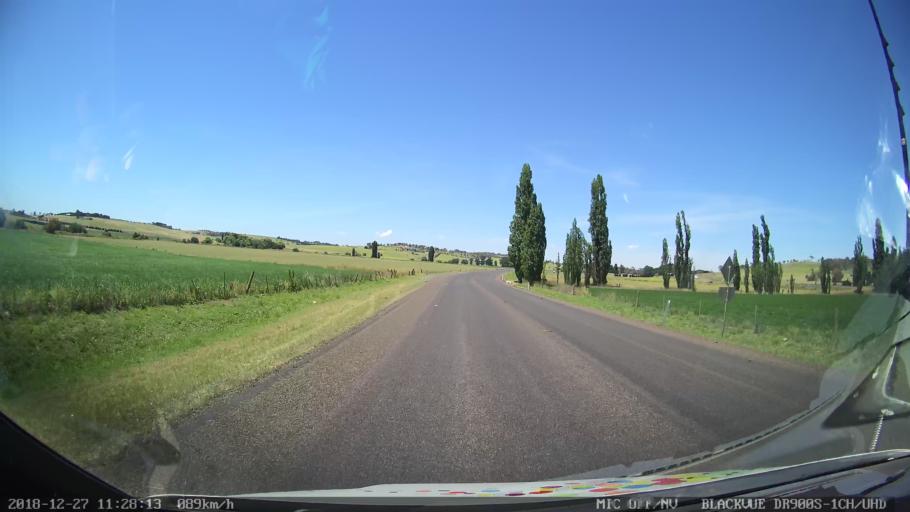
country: AU
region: New South Wales
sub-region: Bathurst Regional
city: Perthville
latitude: -33.4729
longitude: 149.5648
